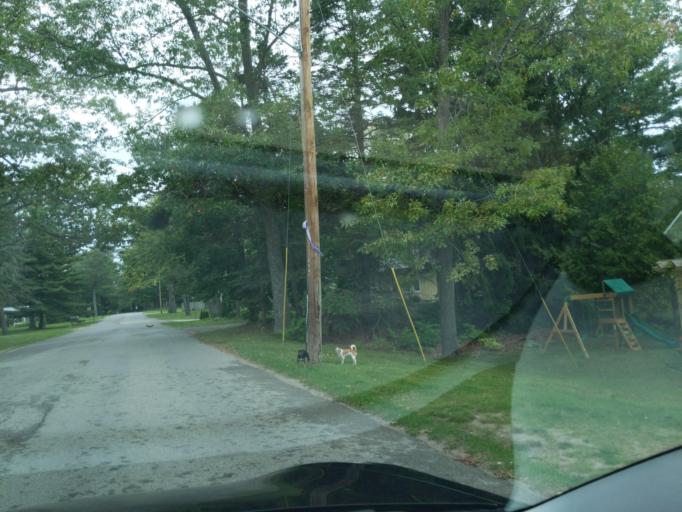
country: US
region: Michigan
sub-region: Grand Traverse County
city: Traverse City
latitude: 44.7518
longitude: -85.5716
